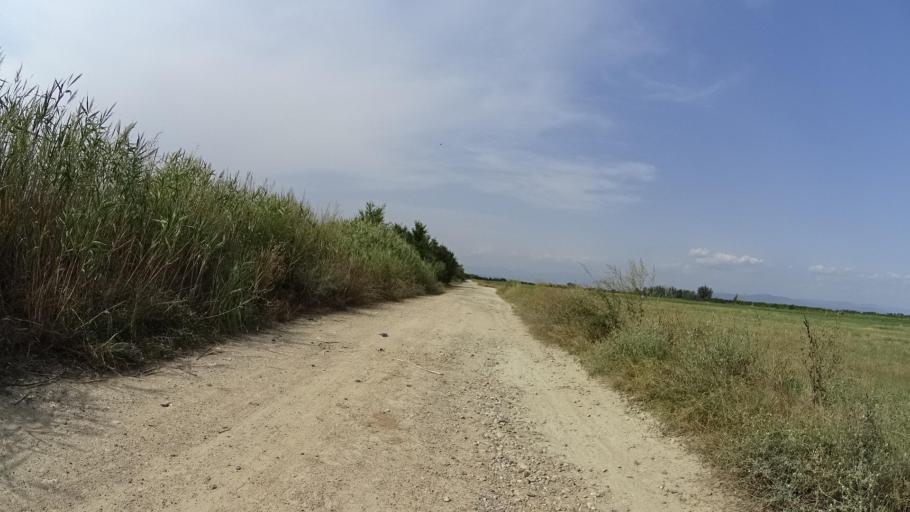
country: BG
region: Plovdiv
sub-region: Obshtina Kaloyanovo
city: Kaloyanovo
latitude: 42.2909
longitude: 24.7965
